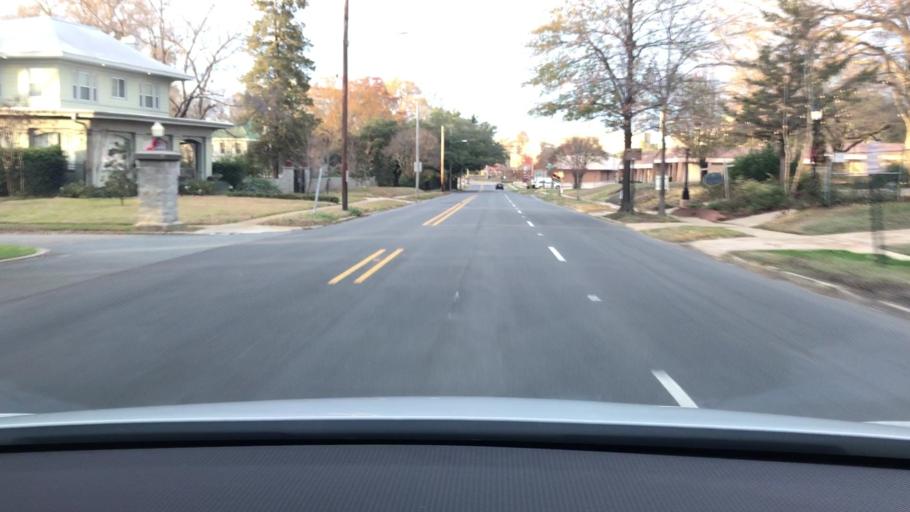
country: US
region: Louisiana
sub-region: Bossier Parish
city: Bossier City
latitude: 32.4900
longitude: -93.7505
